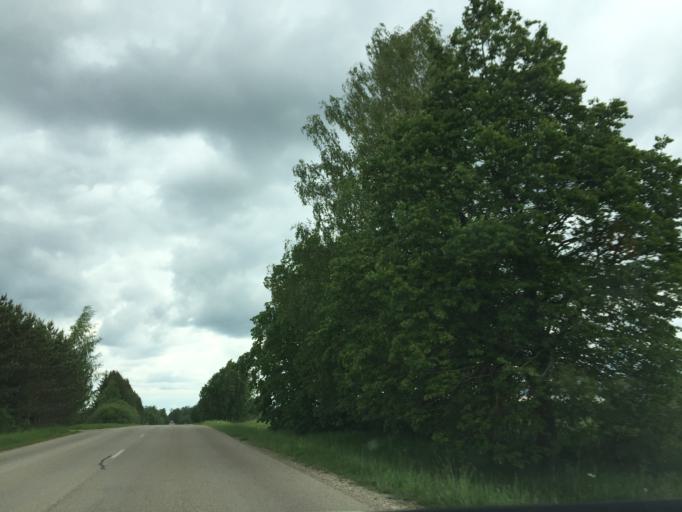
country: LV
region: Dagda
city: Dagda
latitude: 56.1113
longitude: 27.4851
